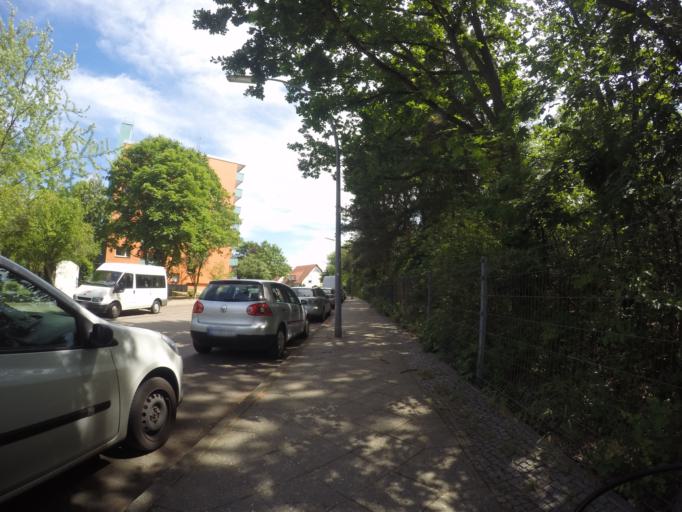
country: DE
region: Berlin
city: Mariendorf
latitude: 52.4385
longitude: 13.3977
